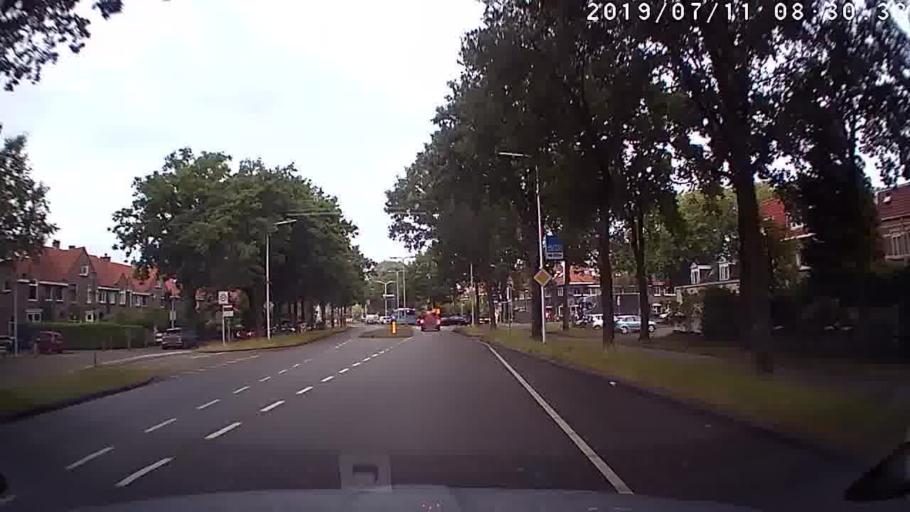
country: NL
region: Overijssel
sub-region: Gemeente Zwolle
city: Zwolle
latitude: 52.5130
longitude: 6.1122
